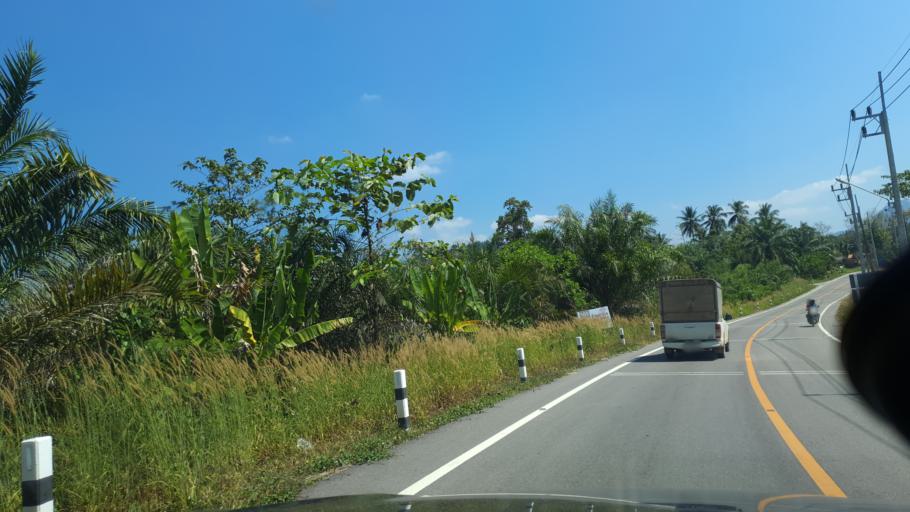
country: TH
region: Krabi
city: Khlong Thom
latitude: 7.9305
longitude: 99.2288
